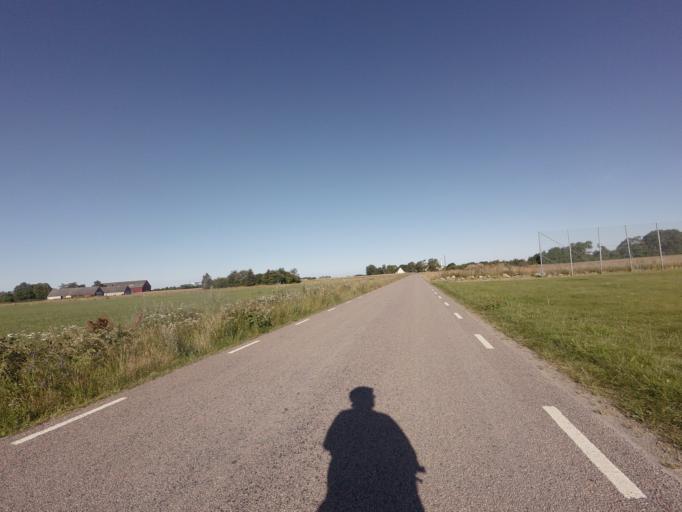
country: SE
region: Skane
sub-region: Hoganas Kommun
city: Hoganas
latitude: 56.1643
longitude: 12.5998
